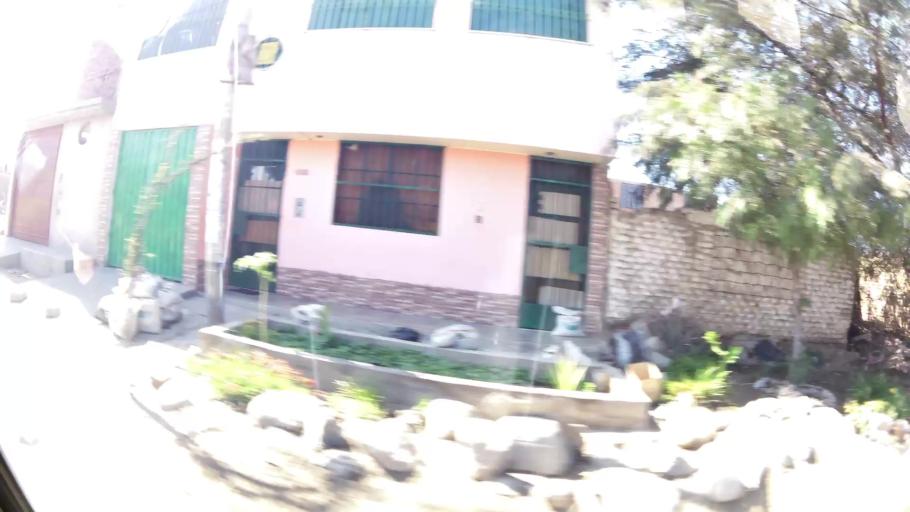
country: PE
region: Ica
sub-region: Provincia de Ica
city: La Tinguina
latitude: -14.0310
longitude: -75.7092
